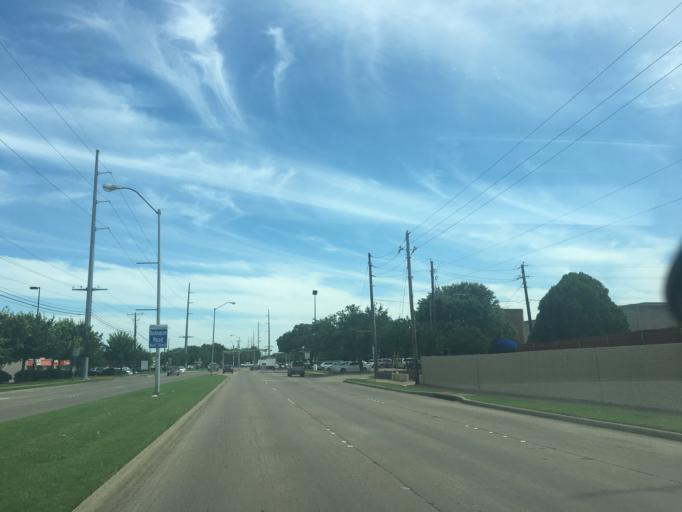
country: US
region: Texas
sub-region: Dallas County
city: Garland
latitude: 32.9334
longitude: -96.6828
